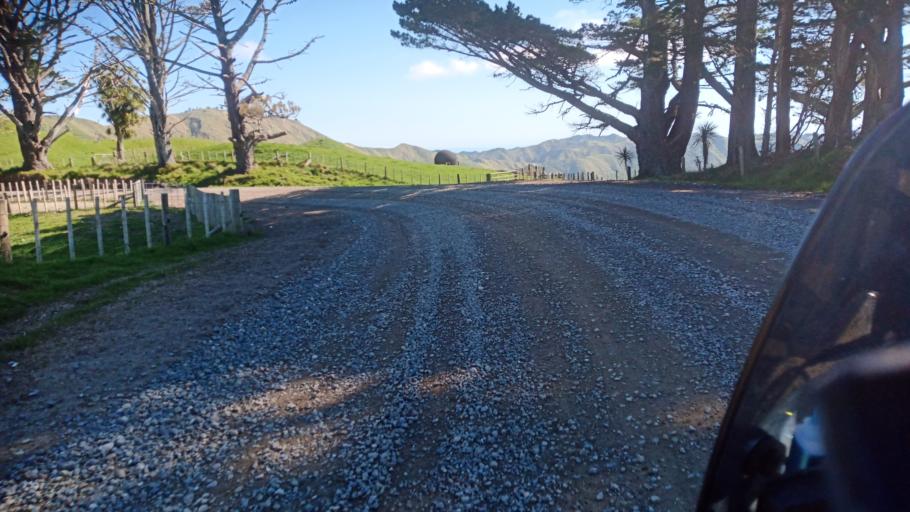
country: NZ
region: Gisborne
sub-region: Gisborne District
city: Gisborne
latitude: -39.1615
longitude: 177.9024
